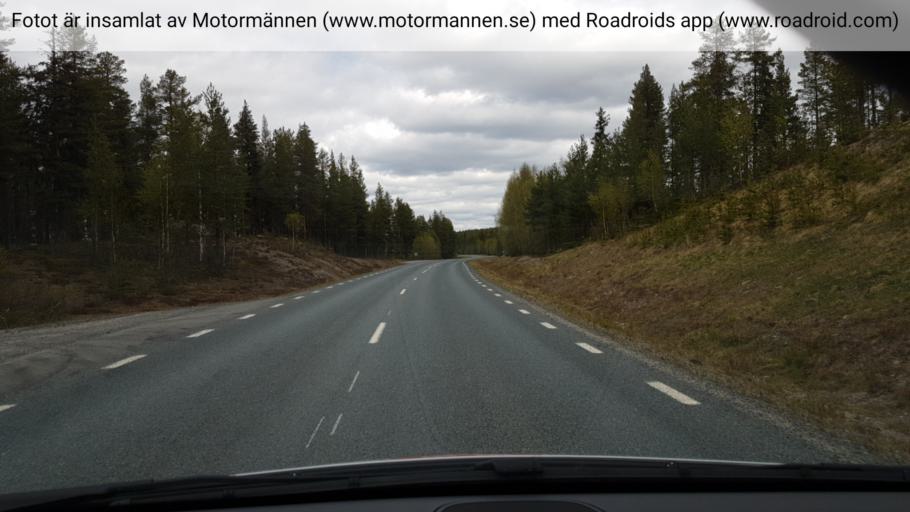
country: SE
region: Vaesterbotten
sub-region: Lycksele Kommun
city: Soderfors
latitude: 65.1776
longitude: 18.2426
